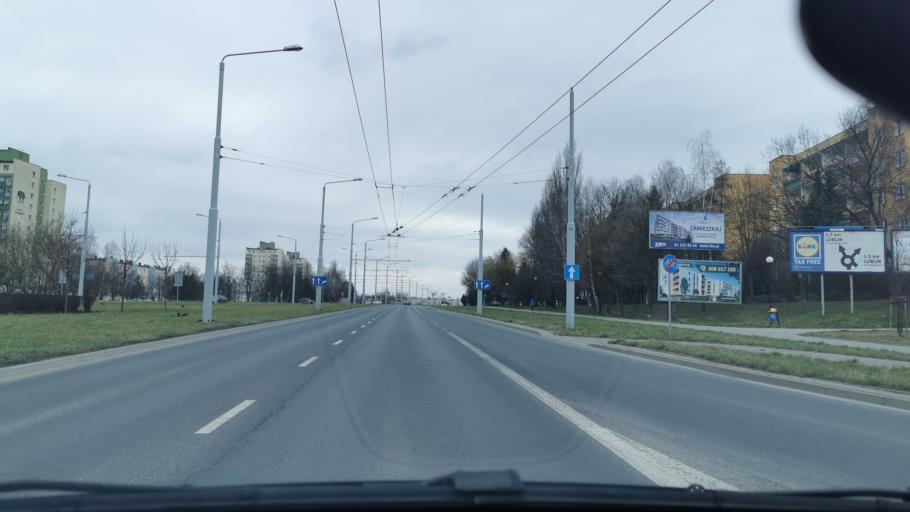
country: PL
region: Lublin Voivodeship
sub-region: Powiat lubelski
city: Lublin
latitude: 51.2270
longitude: 22.5237
